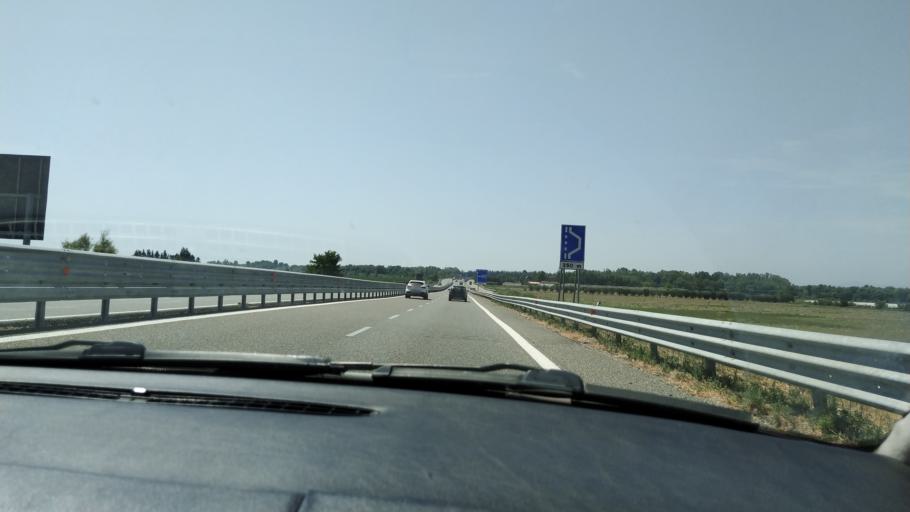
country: IT
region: Basilicate
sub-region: Provincia di Matera
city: Marconia
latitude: 40.3736
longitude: 16.7864
